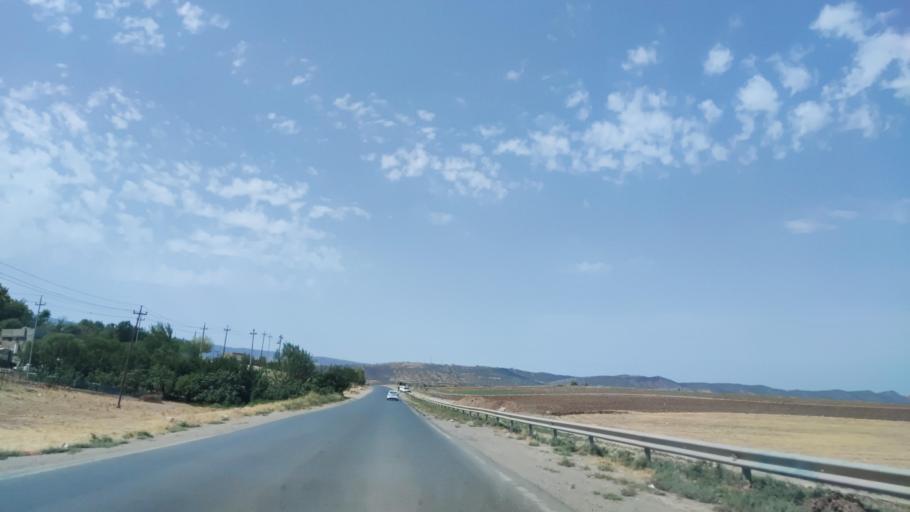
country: IQ
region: Arbil
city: Shaqlawah
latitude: 36.4649
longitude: 44.3944
